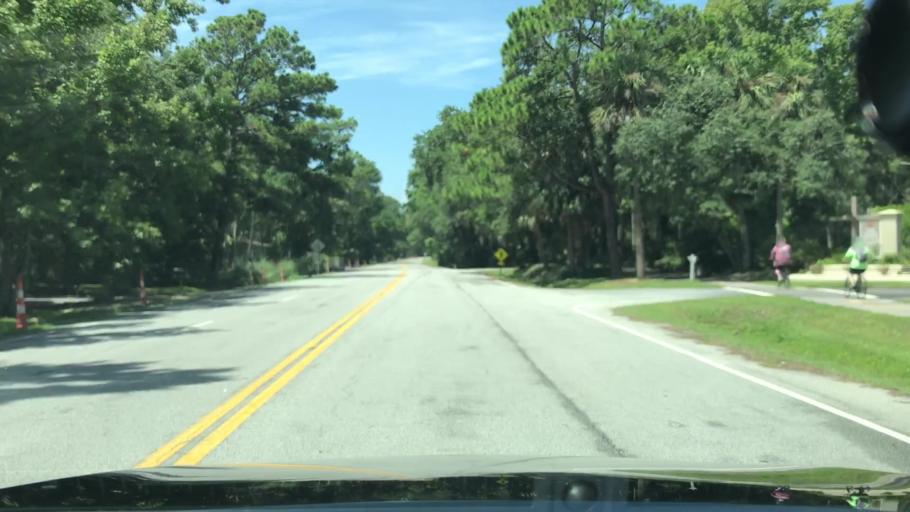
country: US
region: South Carolina
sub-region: Beaufort County
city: Hilton Head Island
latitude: 32.1363
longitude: -80.7664
